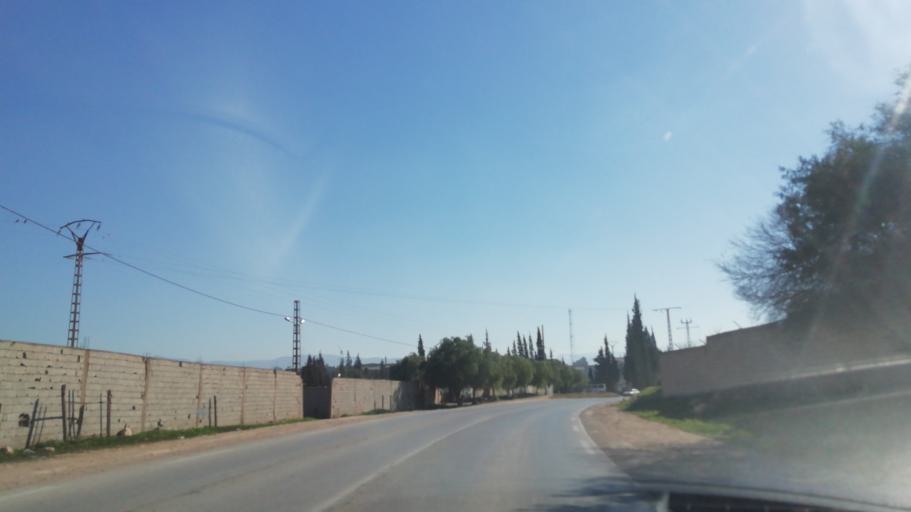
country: DZ
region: Tlemcen
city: Nedroma
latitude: 34.8398
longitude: -1.7040
